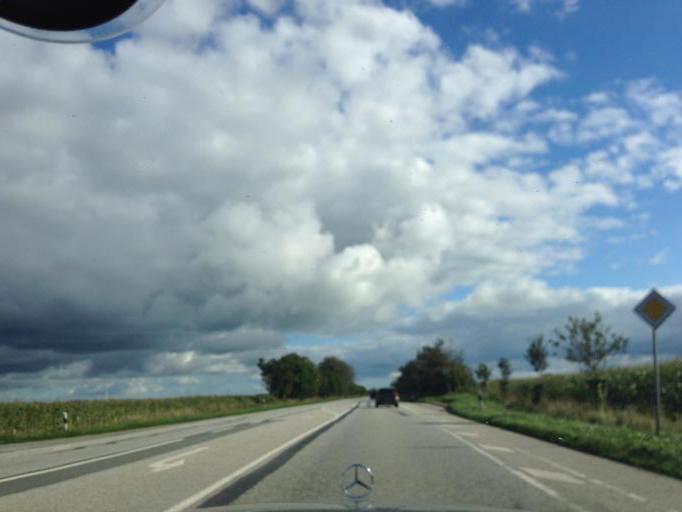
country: DE
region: Schleswig-Holstein
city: Stedesand
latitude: 54.7483
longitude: 8.9120
